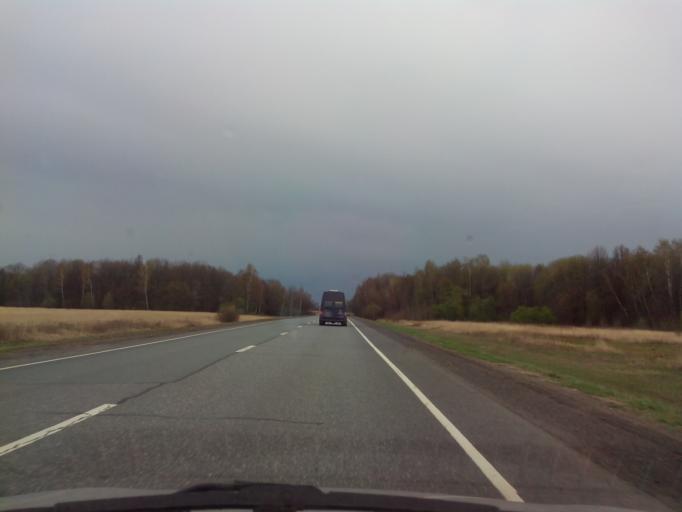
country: RU
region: Moskovskaya
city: Uzunovo
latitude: 54.5587
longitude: 38.4600
